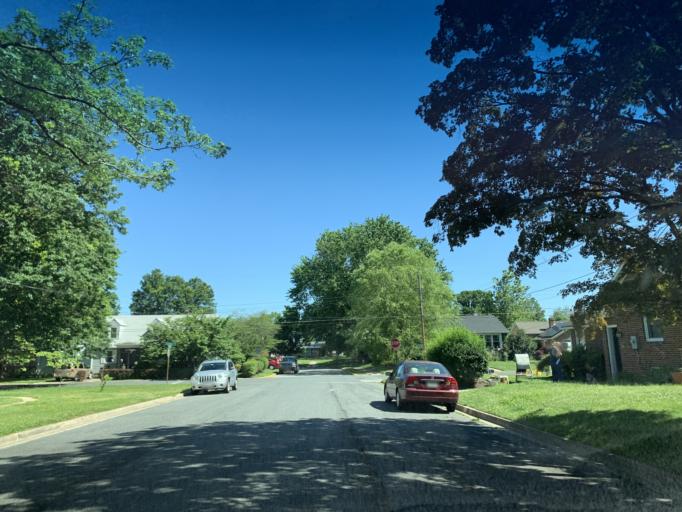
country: US
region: Maryland
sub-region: Harford County
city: Havre de Grace
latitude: 39.5401
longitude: -76.0969
